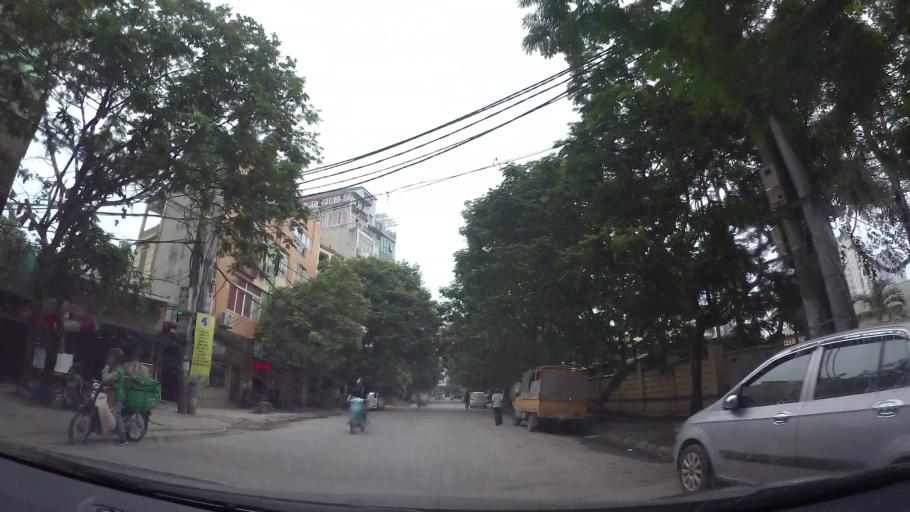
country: VN
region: Ha Noi
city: Hai BaTrung
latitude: 20.9861
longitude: 105.8564
